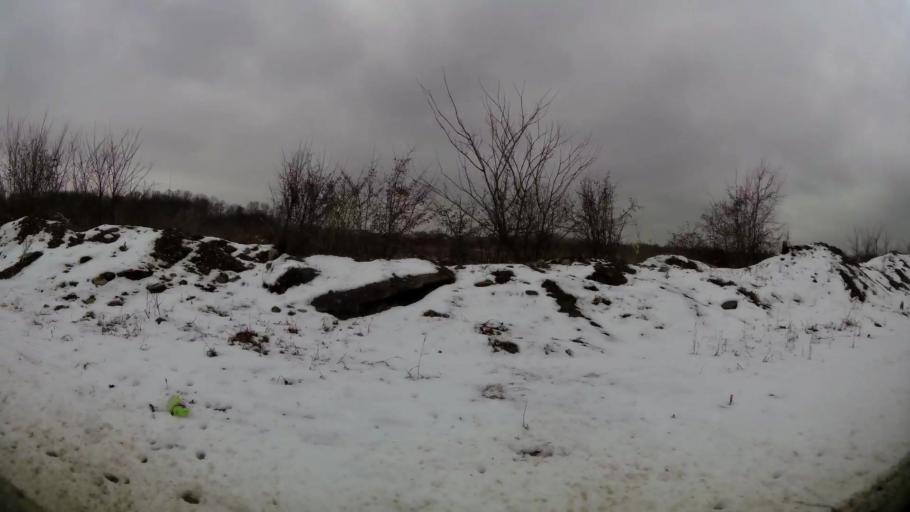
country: RO
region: Ilfov
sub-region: Comuna Mogosoaia
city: Mogosoaia
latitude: 44.5064
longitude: 26.0082
